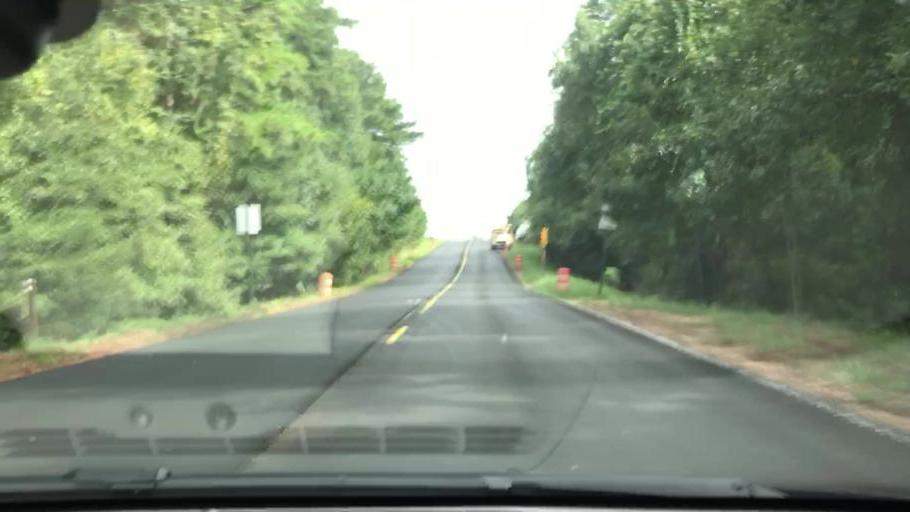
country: US
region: Georgia
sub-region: Clay County
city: Fort Gaines
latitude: 31.5913
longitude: -85.0334
